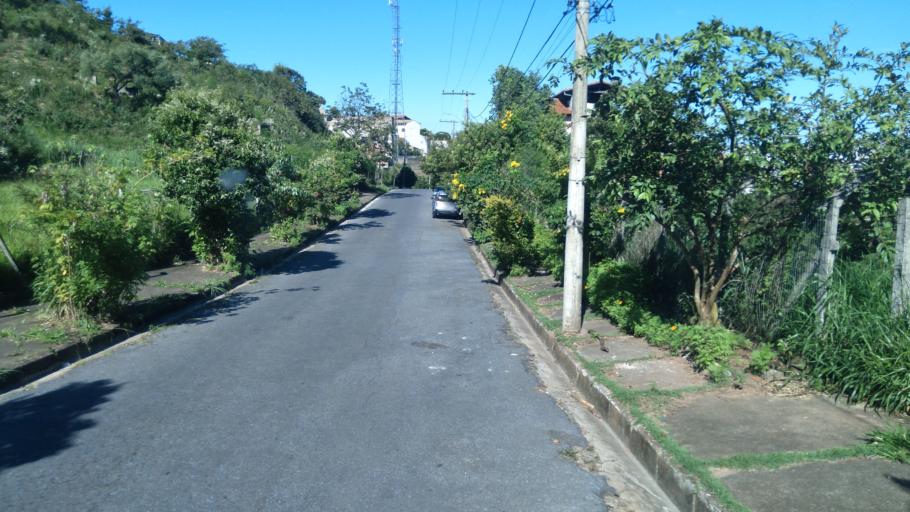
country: BR
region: Minas Gerais
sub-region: Belo Horizonte
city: Belo Horizonte
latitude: -19.9203
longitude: -43.8927
